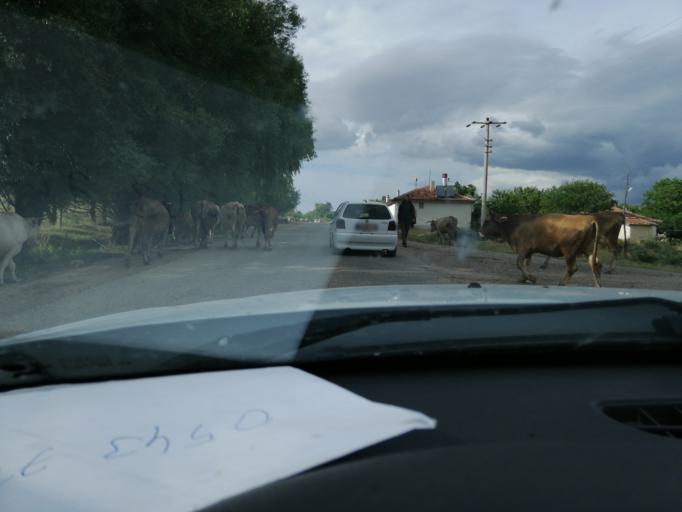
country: TR
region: Kirsehir
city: Kirsehir
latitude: 39.0229
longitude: 34.1241
